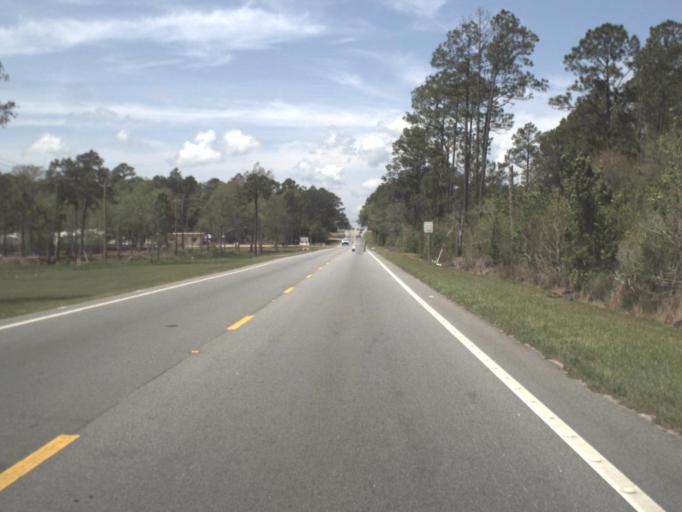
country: US
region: Florida
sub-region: Escambia County
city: Cantonment
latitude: 30.5355
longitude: -87.3728
